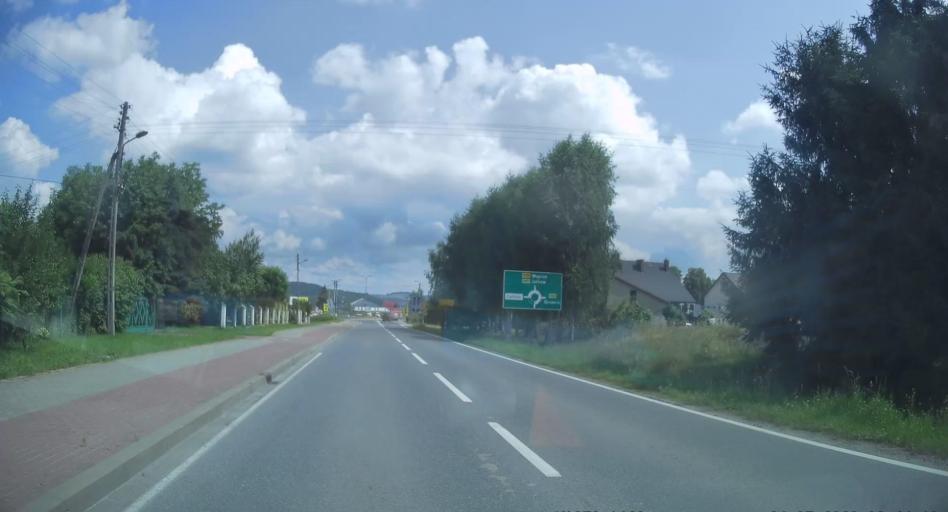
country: PL
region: Lesser Poland Voivodeship
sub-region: Powiat tarnowski
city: Zakliczyn
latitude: 49.8547
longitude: 20.8129
